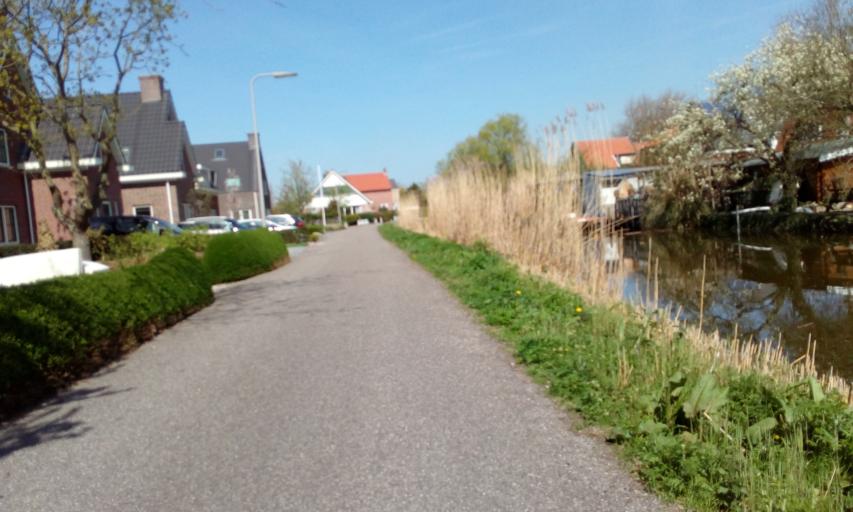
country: NL
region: South Holland
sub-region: Gemeente Delft
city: Delft
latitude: 52.0063
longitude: 4.3264
